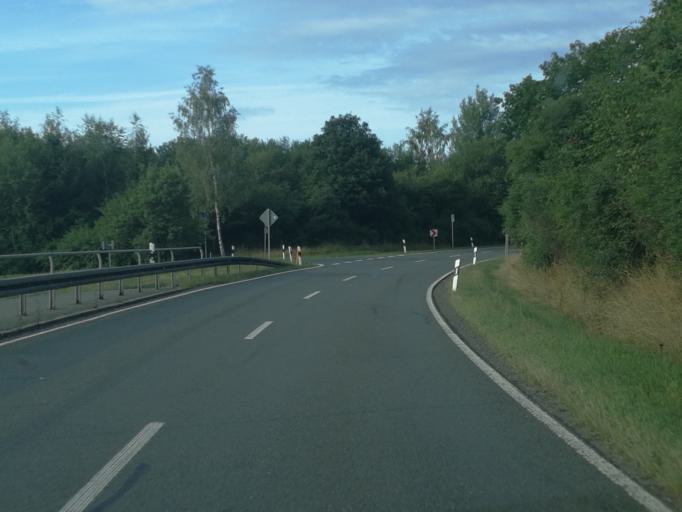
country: DE
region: Bavaria
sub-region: Upper Franconia
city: Regnitzlosau
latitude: 50.3145
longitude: 12.0529
